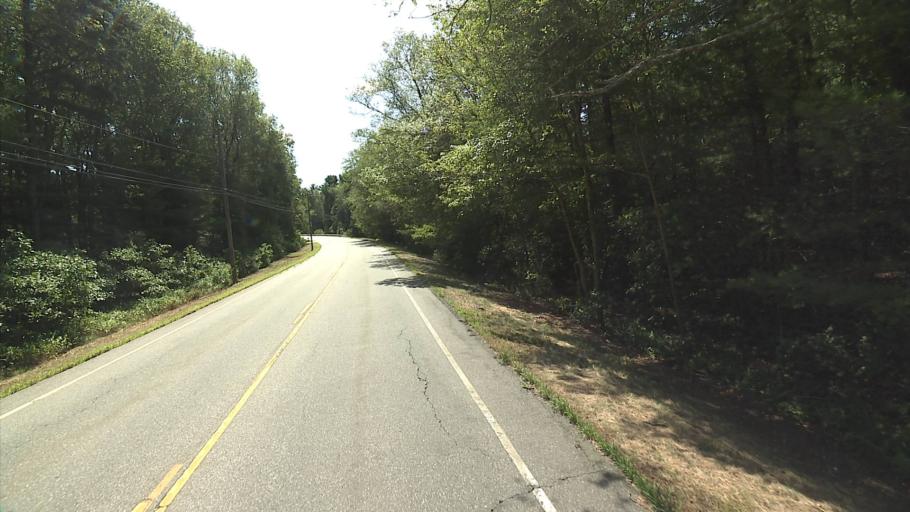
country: US
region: Rhode Island
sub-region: Washington County
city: Hopkinton
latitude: 41.5660
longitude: -71.8274
